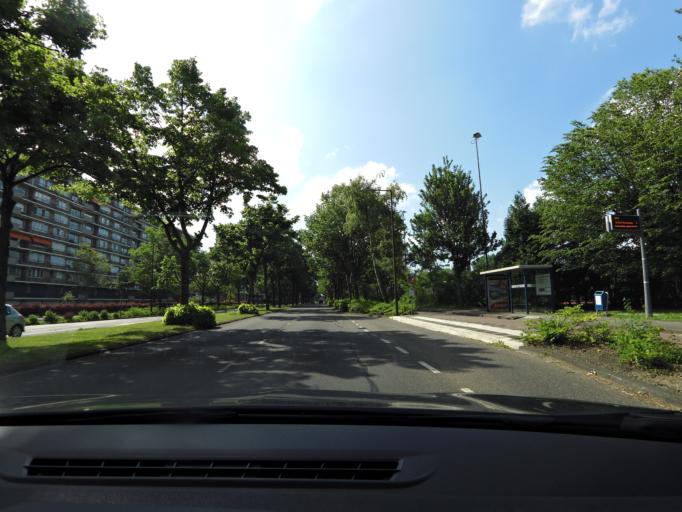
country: NL
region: South Holland
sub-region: Gemeente Vlaardingen
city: Vlaardingen
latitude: 51.9274
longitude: 4.3443
